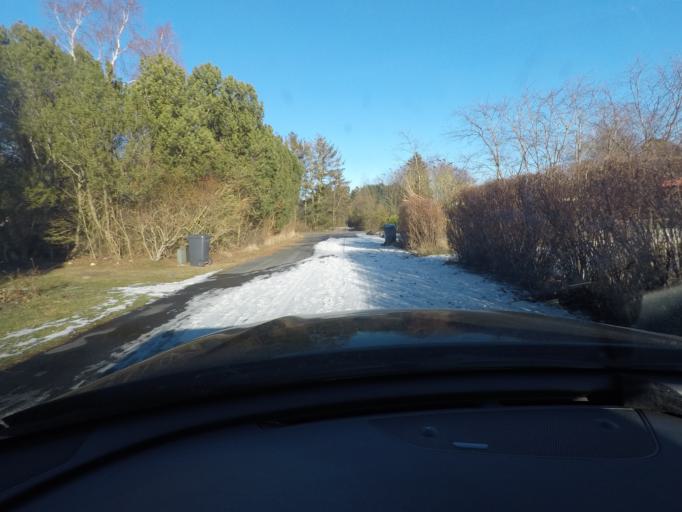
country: DK
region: Capital Region
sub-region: Halsnaes Kommune
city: Liseleje
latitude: 55.9952
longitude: 11.9397
